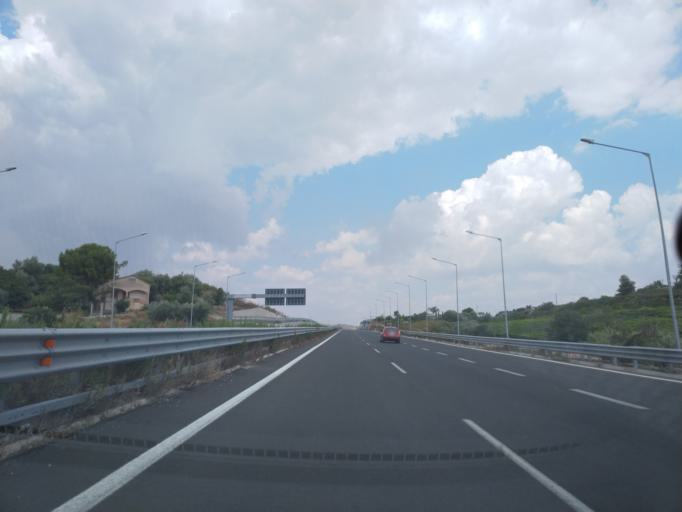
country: IT
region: Sicily
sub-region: Agrigento
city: Racalmuto
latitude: 37.3862
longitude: 13.7397
